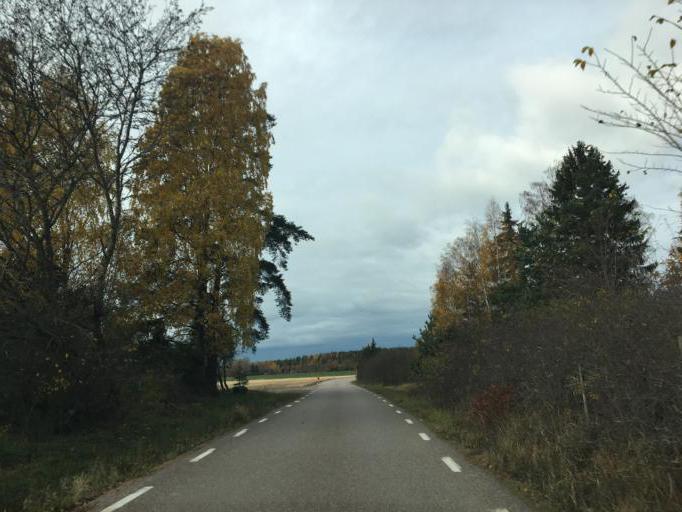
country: SE
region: Vaestmanland
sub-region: Hallstahammars Kommun
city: Kolback
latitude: 59.5491
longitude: 16.3457
